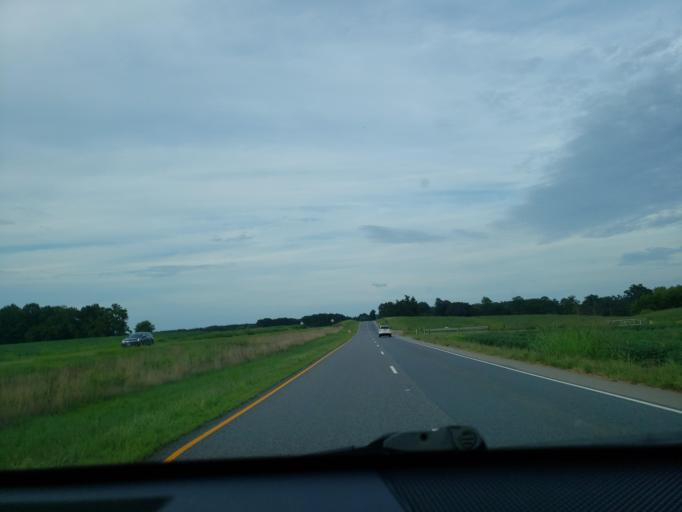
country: US
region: Virginia
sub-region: Brunswick County
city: Lawrenceville
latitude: 36.7196
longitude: -77.9643
